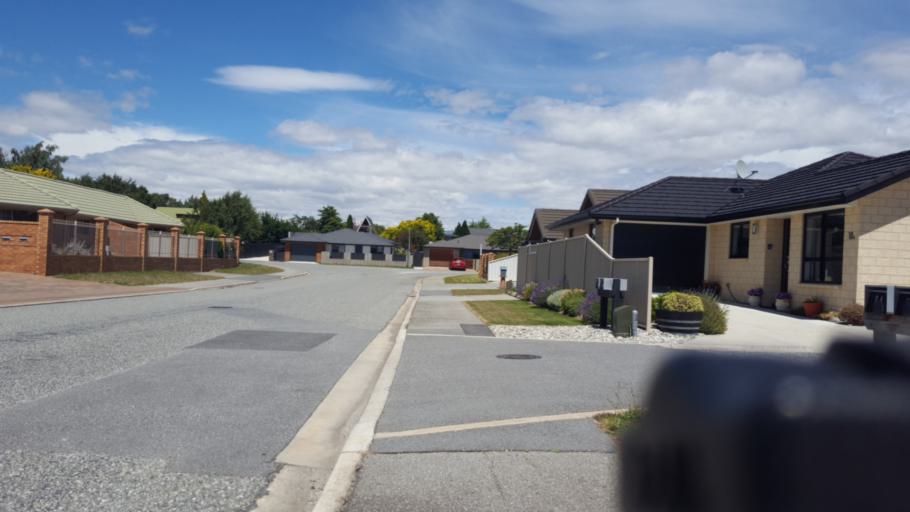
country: NZ
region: Otago
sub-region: Queenstown-Lakes District
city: Wanaka
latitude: -45.0390
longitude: 169.1996
